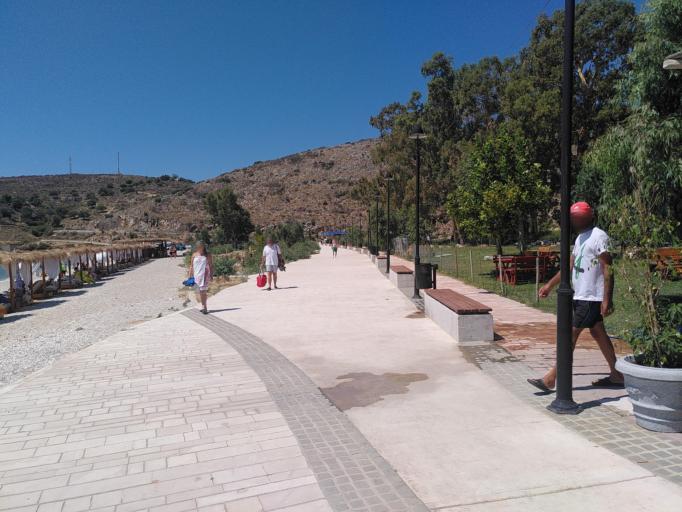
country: AL
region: Vlore
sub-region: Rrethi i Vlores
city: Himare
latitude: 40.0522
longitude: 19.8158
